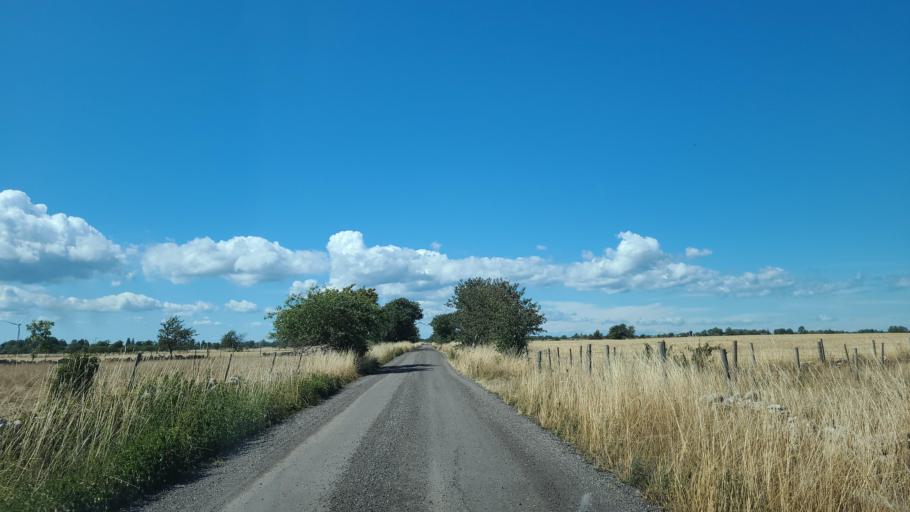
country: SE
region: Kalmar
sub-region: Morbylanga Kommun
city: Sodra Sandby
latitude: 56.7087
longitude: 16.7259
